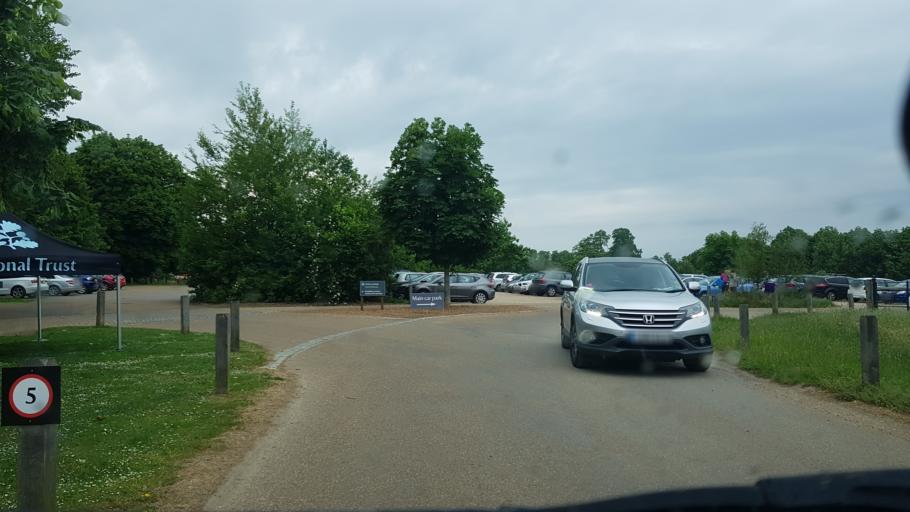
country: GB
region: England
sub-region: Surrey
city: Great Bookham
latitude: 51.2596
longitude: -0.3739
